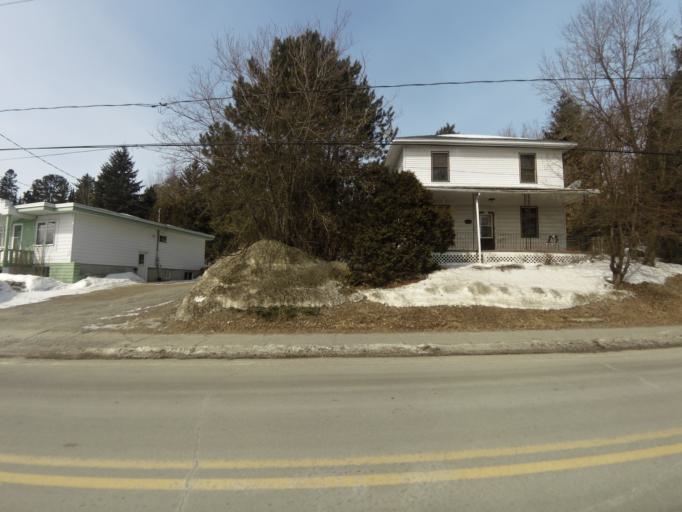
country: CA
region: Quebec
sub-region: Laurentides
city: Mont-Laurier
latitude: 46.5560
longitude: -75.5014
